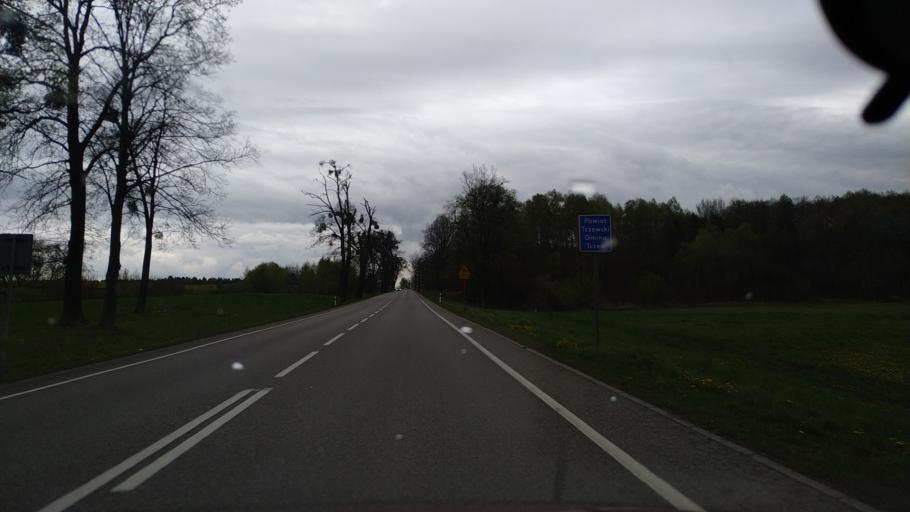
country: PL
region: Pomeranian Voivodeship
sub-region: Powiat tczewski
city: Pelplin
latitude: 54.0192
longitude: 18.6300
